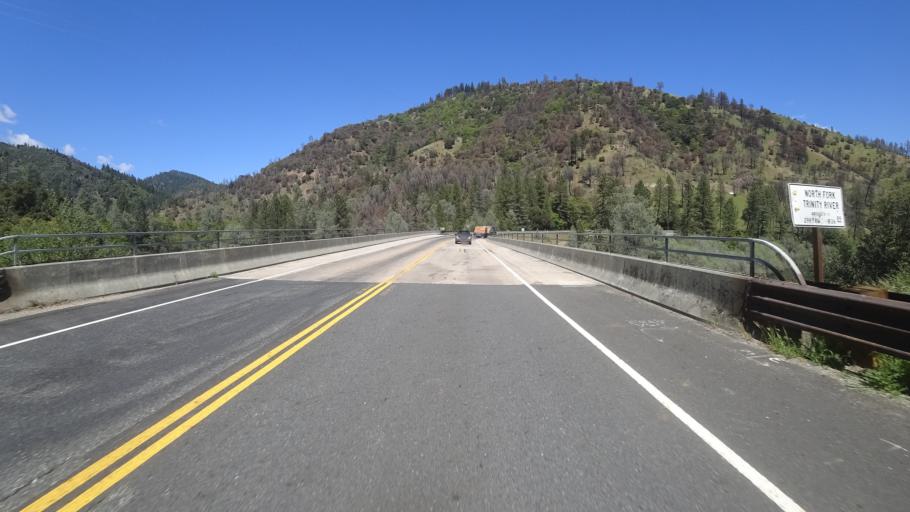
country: US
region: California
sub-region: Trinity County
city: Weaverville
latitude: 40.7697
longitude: -123.1281
